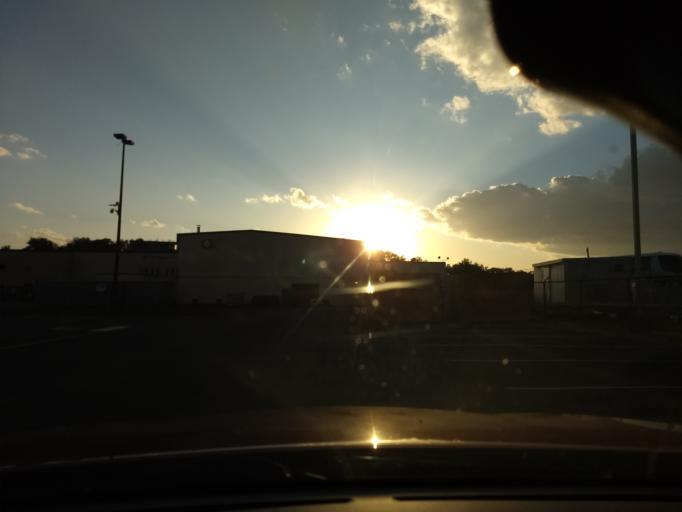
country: US
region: Pennsylvania
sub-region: Allegheny County
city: Pleasant Hills
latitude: 40.3483
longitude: -79.9558
